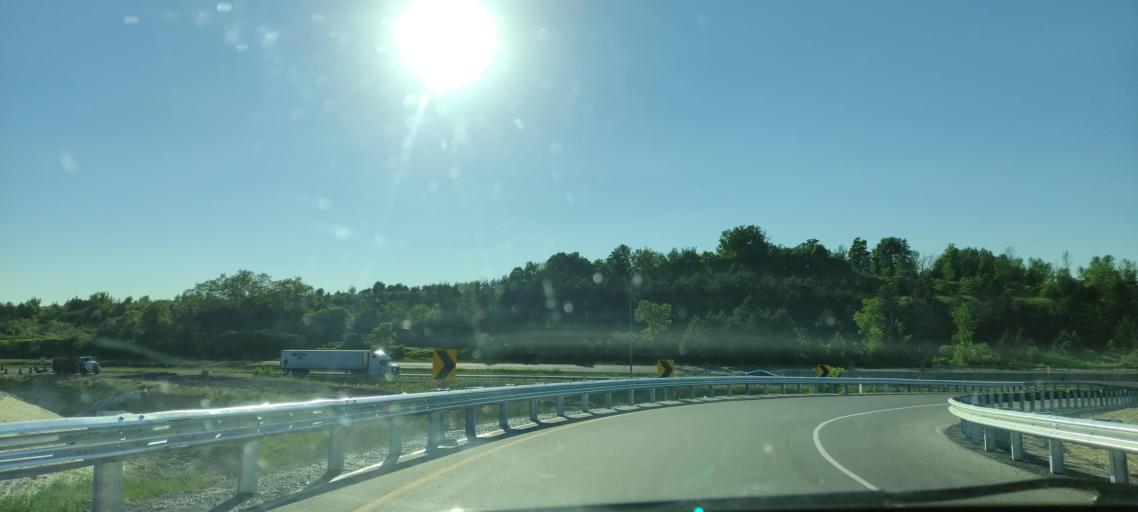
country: CA
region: Ontario
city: Quinte West
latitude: 44.0730
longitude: -77.7693
